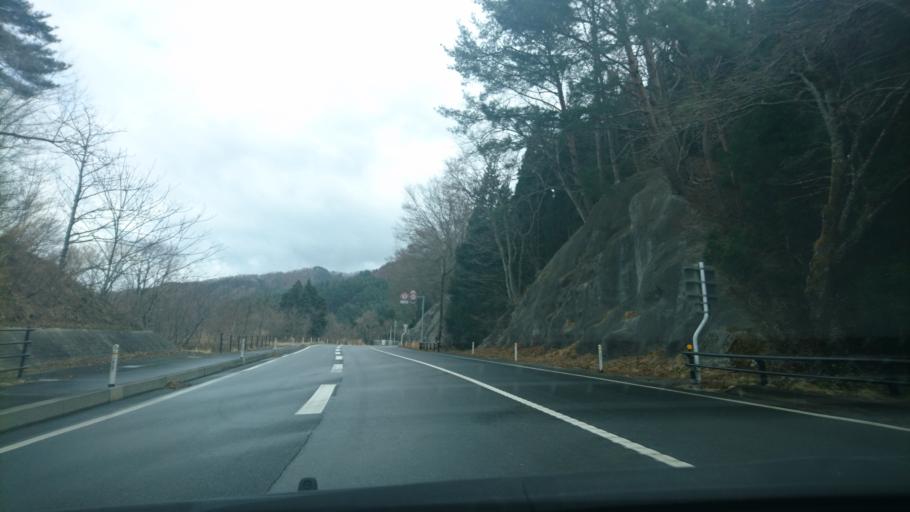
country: JP
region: Iwate
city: Ofunato
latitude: 39.1359
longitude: 141.8212
